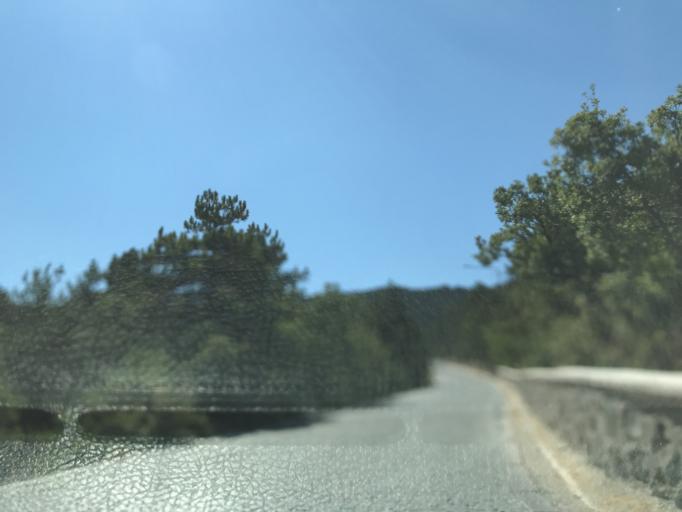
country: TR
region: Yozgat
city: Yozgat
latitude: 39.8084
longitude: 34.8087
